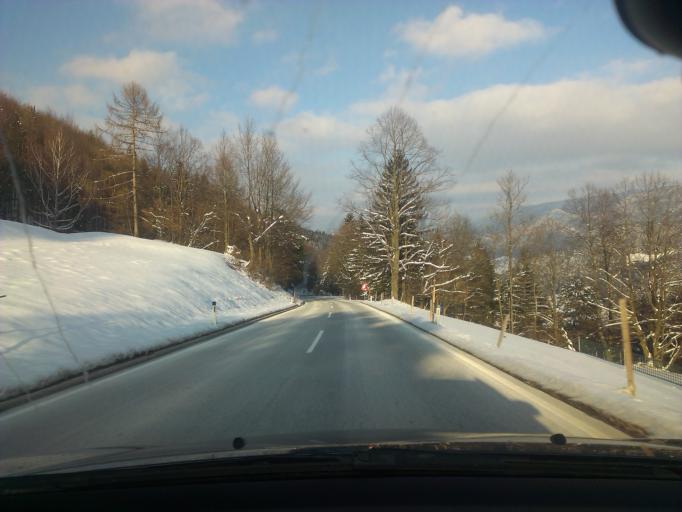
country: AT
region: Lower Austria
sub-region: Politischer Bezirk Neunkirchen
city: Puchberg am Schneeberg
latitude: 47.8166
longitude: 15.9443
